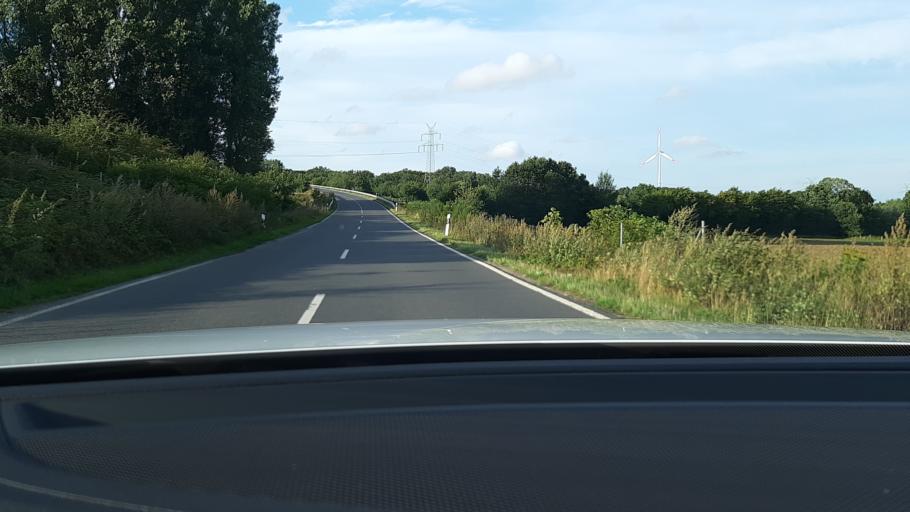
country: DE
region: Schleswig-Holstein
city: Monkhagen
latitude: 53.9076
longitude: 10.5524
